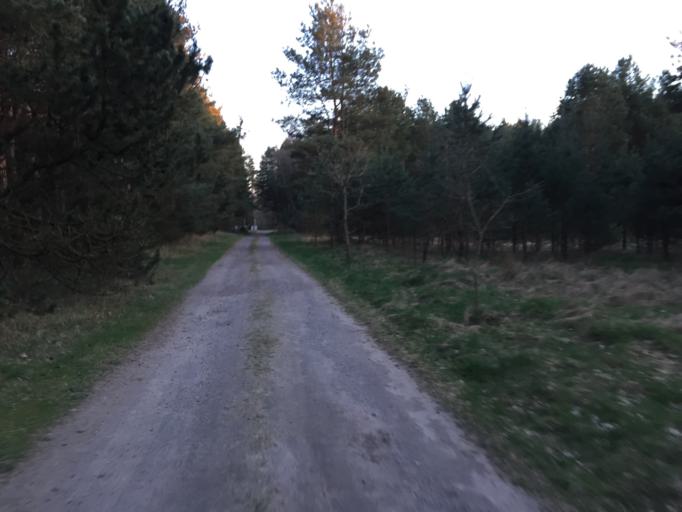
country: SE
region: Skane
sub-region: Lunds Kommun
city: Veberod
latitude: 55.6364
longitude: 13.5115
